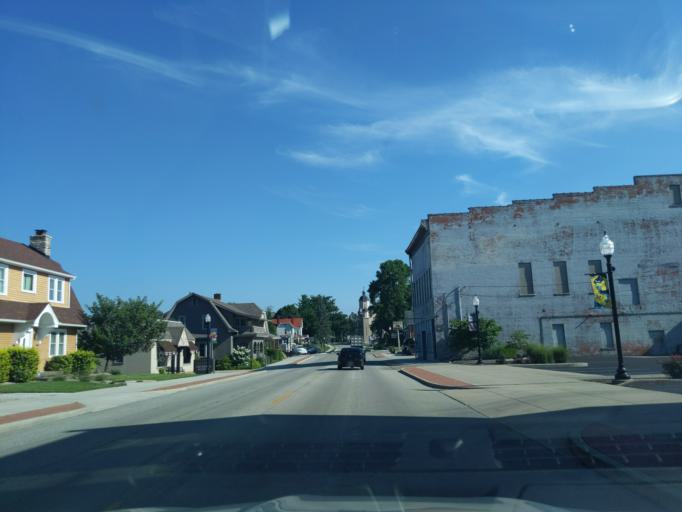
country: US
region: Indiana
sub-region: Ripley County
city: Osgood
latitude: 39.1292
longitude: -85.2914
